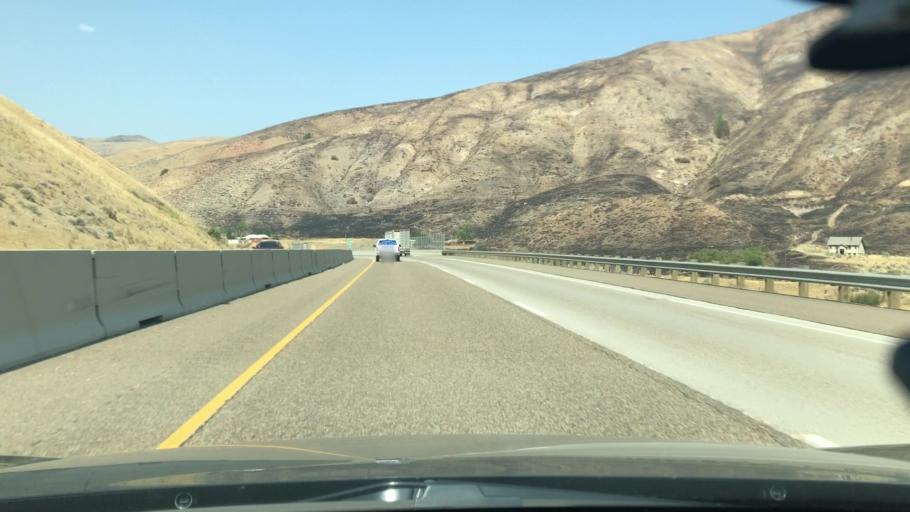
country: US
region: Idaho
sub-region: Washington County
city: Weiser
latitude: 44.4104
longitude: -117.3102
